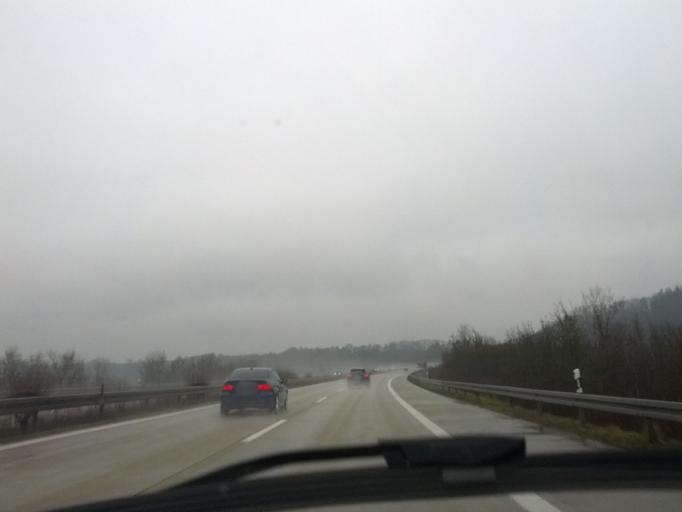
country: DE
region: Bavaria
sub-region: Regierungsbezirk Mittelfranken
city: Diebach
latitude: 49.3191
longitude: 10.2050
